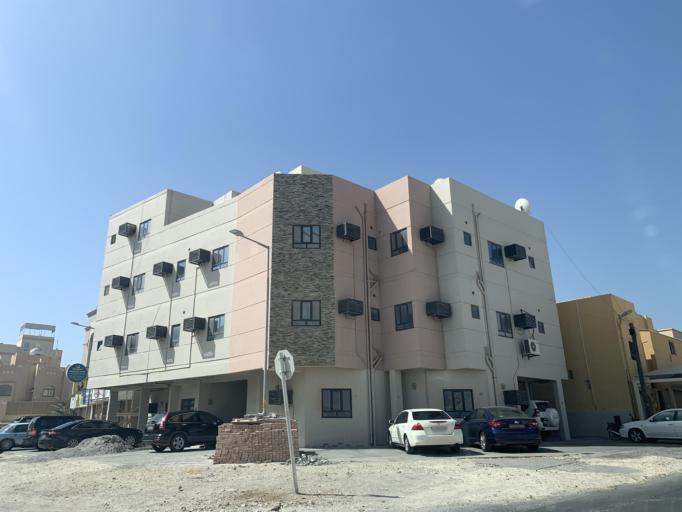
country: BH
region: Northern
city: Ar Rifa'
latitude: 26.1360
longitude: 50.5806
